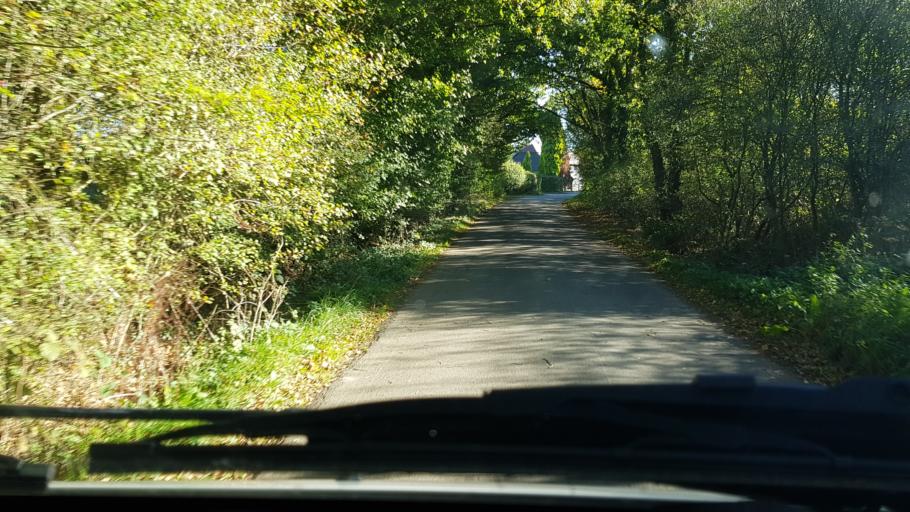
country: GB
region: England
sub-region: Surrey
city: Ockley
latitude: 51.1261
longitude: -0.3638
